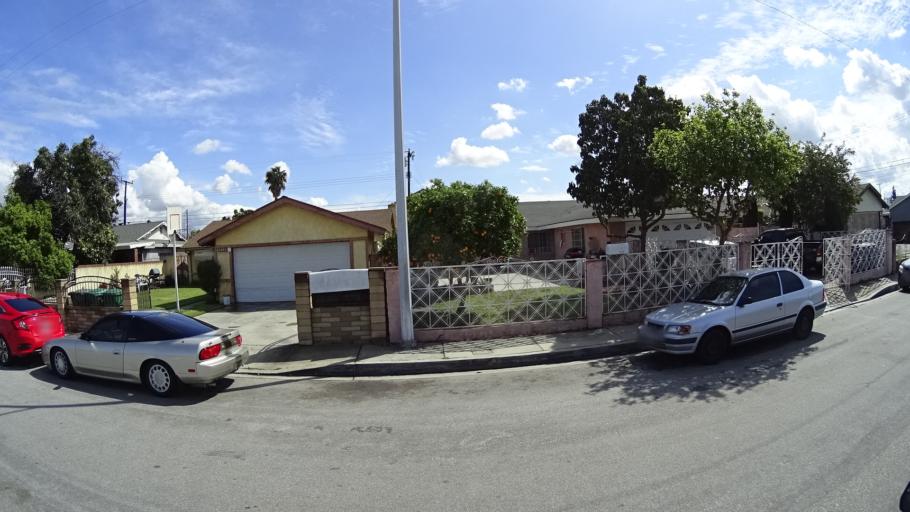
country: US
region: California
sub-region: Los Angeles County
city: Baldwin Park
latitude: 34.0855
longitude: -117.9800
